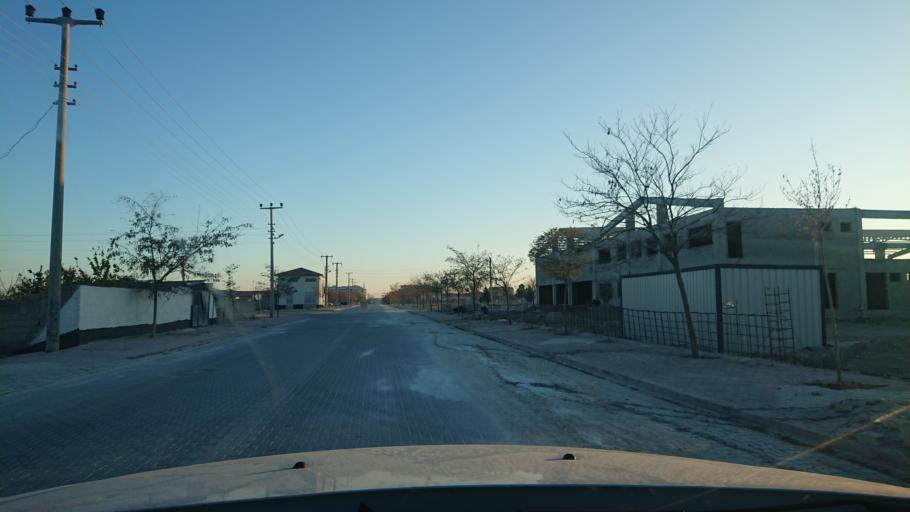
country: TR
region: Aksaray
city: Eskil
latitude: 38.3988
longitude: 33.4202
